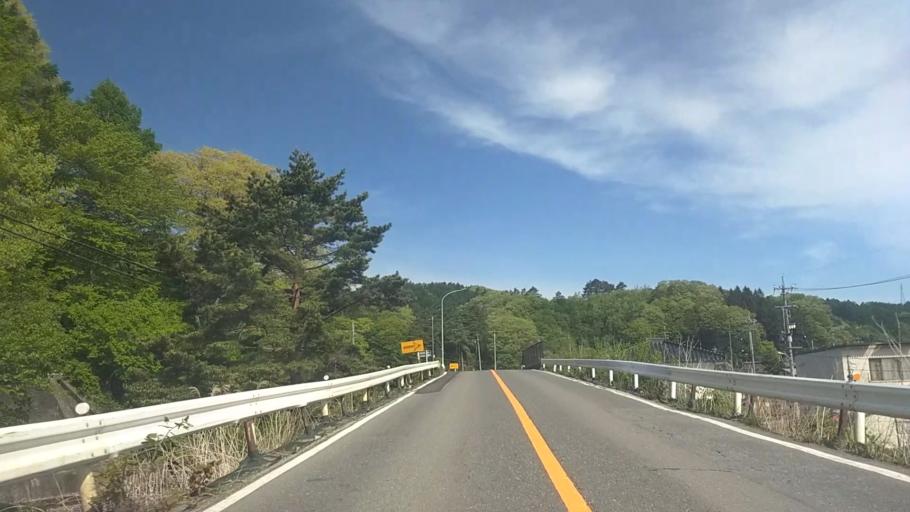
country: JP
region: Nagano
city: Saku
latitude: 36.0377
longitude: 138.4733
